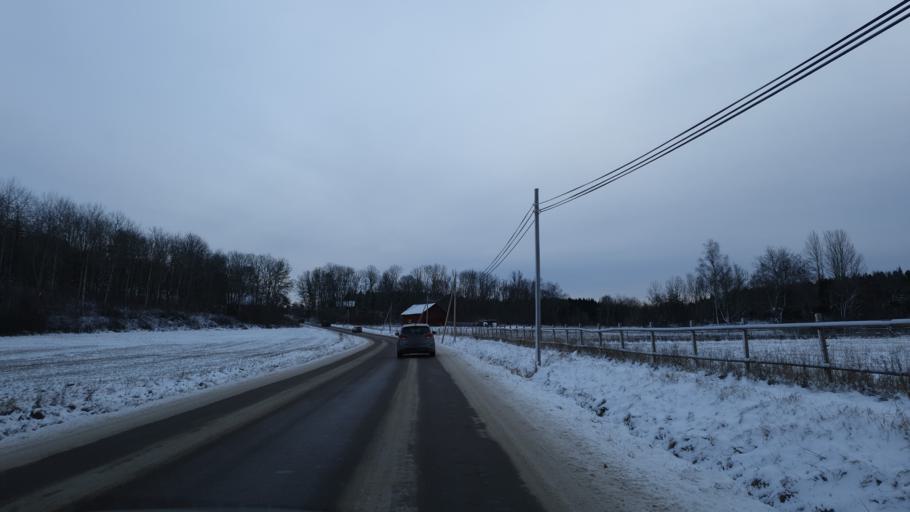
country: SE
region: Uppsala
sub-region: Uppsala Kommun
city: Saevja
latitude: 59.7079
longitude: 17.5926
